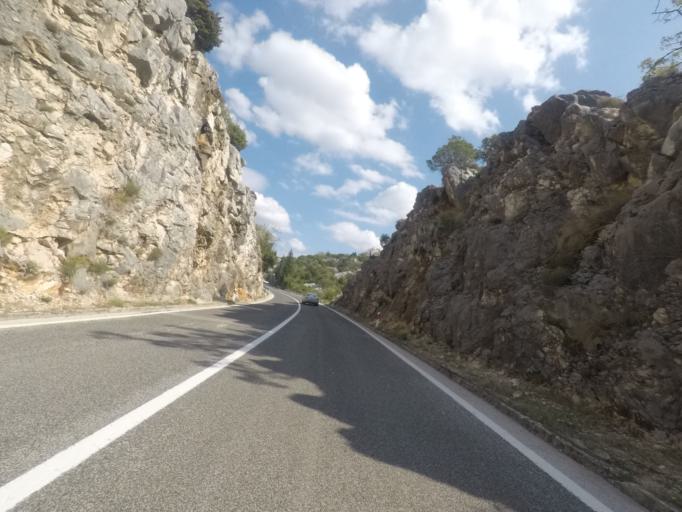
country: HR
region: Dubrovacko-Neretvanska
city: Komin
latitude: 43.0646
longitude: 17.4360
